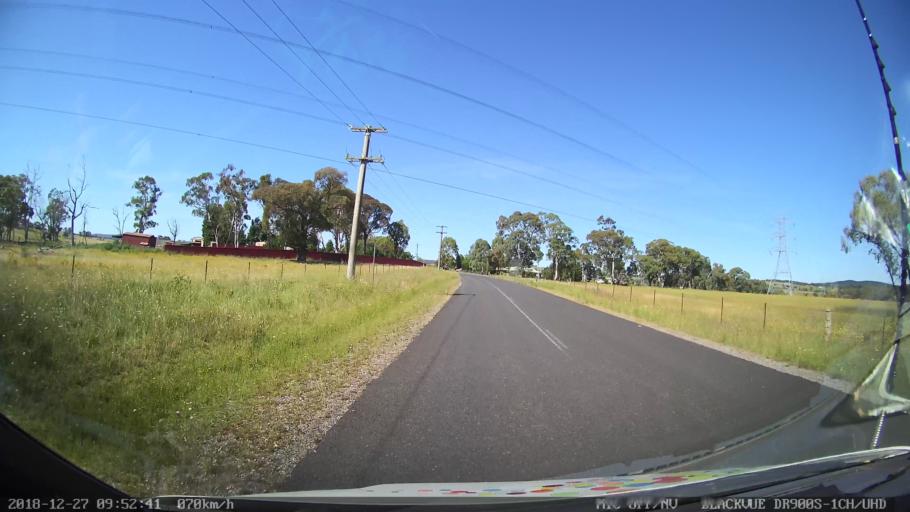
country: AU
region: New South Wales
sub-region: Lithgow
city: Portland
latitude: -33.3752
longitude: 149.9900
